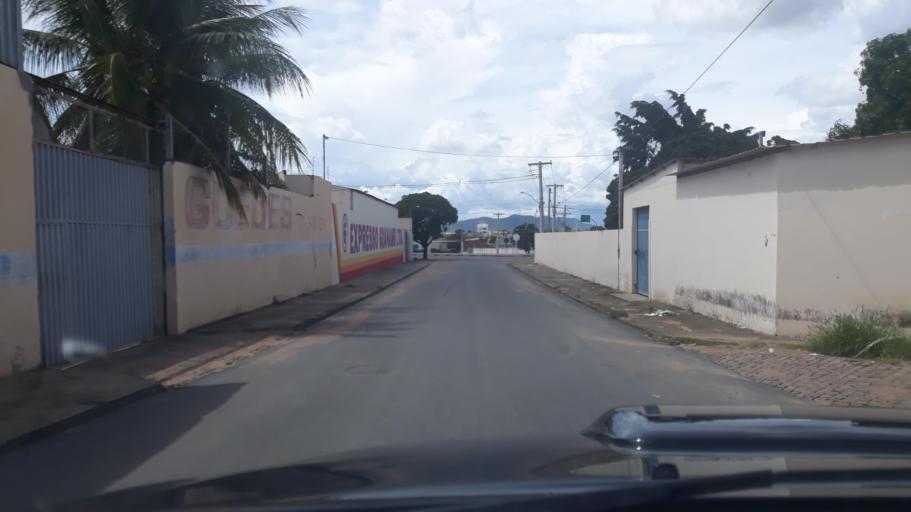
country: BR
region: Bahia
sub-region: Guanambi
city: Guanambi
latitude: -14.2115
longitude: -42.7893
